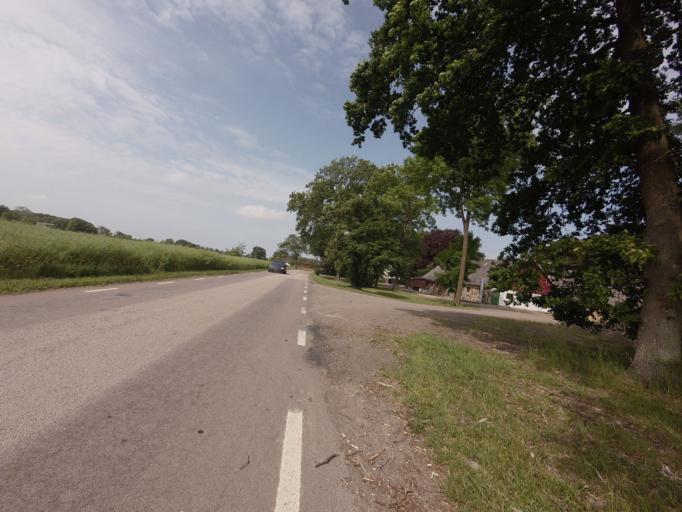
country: SE
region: Skane
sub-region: Helsingborg
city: Odakra
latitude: 56.1831
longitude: 12.6645
